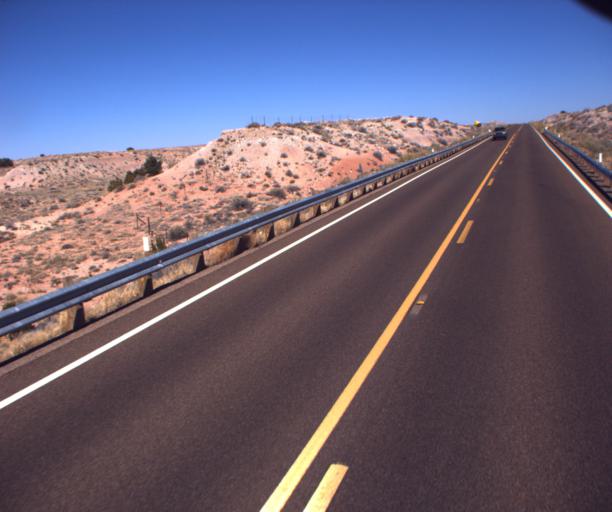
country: US
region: Arizona
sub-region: Navajo County
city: Dilkon
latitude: 35.1880
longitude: -110.4425
